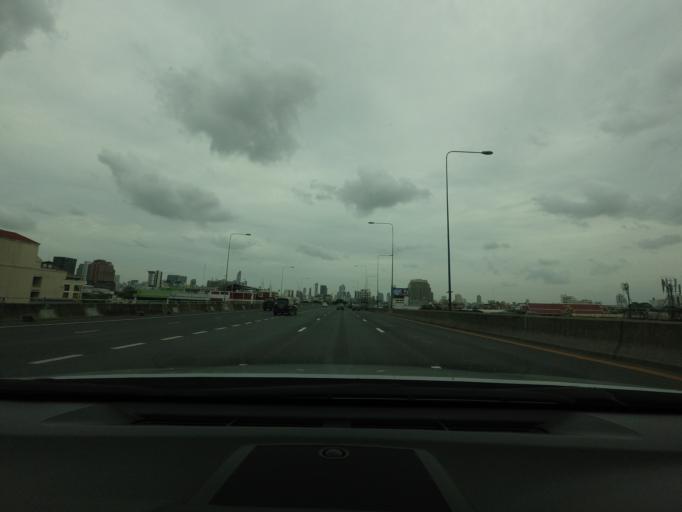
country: TH
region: Bangkok
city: Pom Prap Sattru Phai
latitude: 13.7536
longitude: 100.5231
